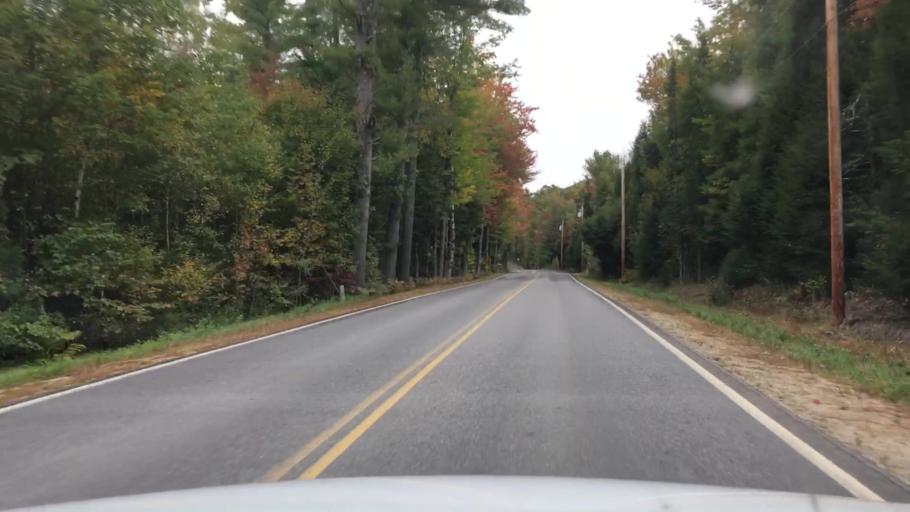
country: US
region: Maine
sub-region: Oxford County
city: Bethel
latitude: 44.2684
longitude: -70.7282
